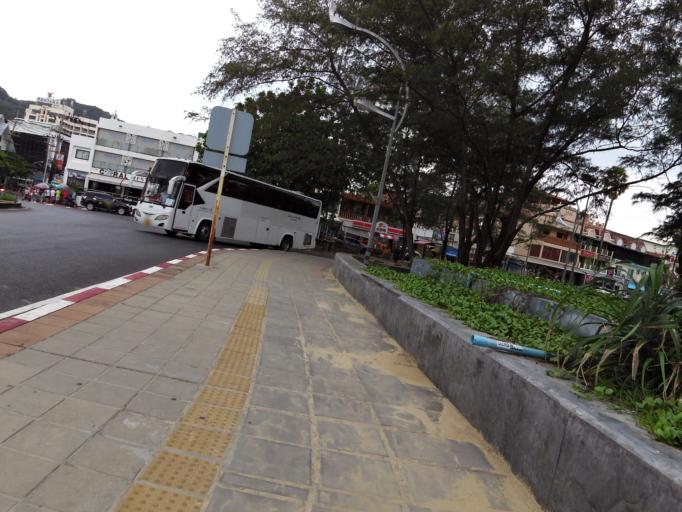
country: TH
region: Phuket
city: Ban Karon
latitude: 7.8488
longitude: 98.2930
